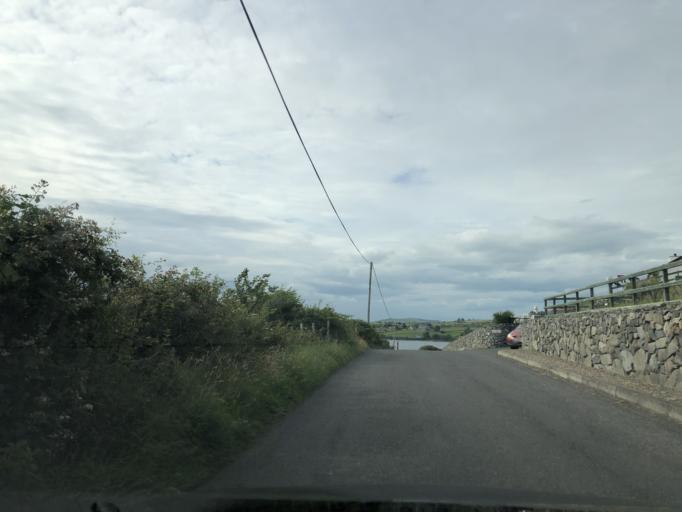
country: GB
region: Northern Ireland
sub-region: Down District
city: Castlewellan
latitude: 54.2323
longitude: -6.0115
